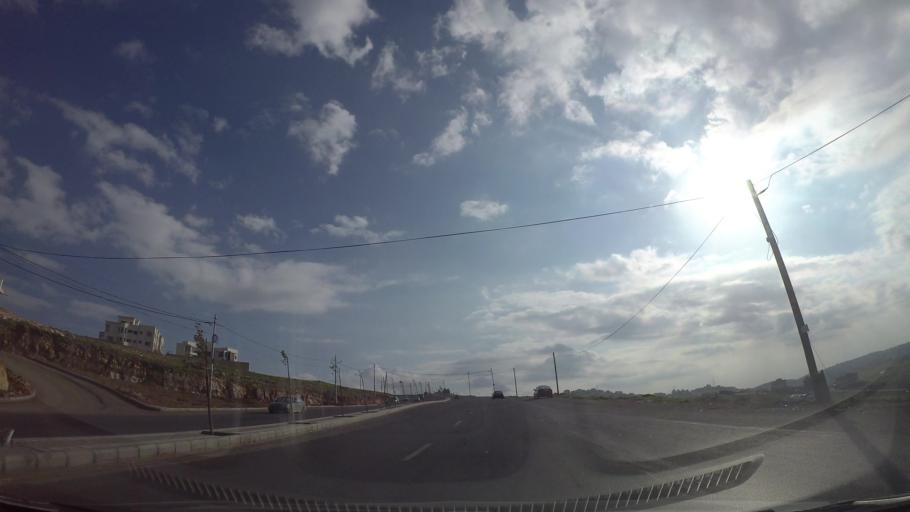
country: JO
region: Amman
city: Wadi as Sir
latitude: 31.9261
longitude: 35.8481
